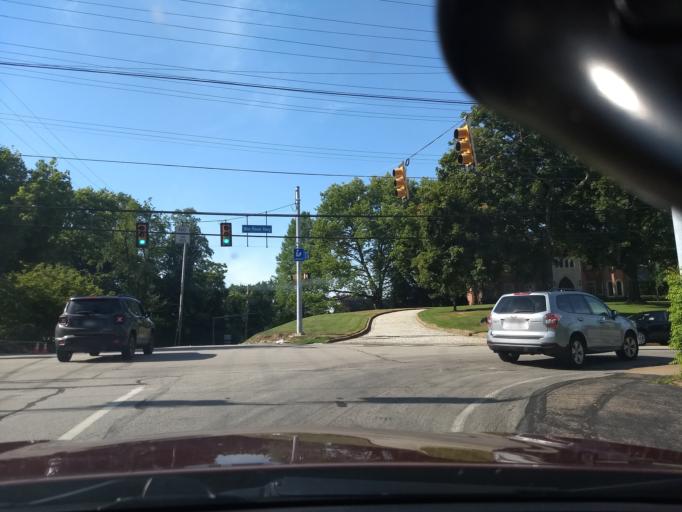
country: US
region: Pennsylvania
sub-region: Allegheny County
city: Churchill
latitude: 40.4450
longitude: -79.8584
